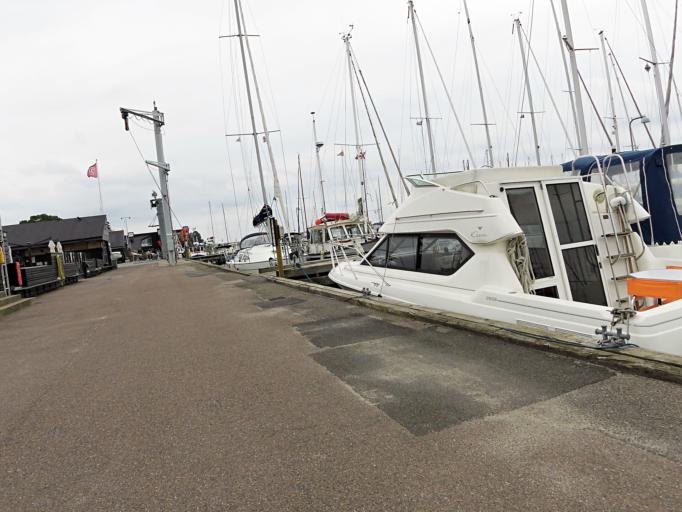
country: DK
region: Capital Region
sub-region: Rudersdal Kommune
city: Trorod
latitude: 55.8493
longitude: 12.5713
